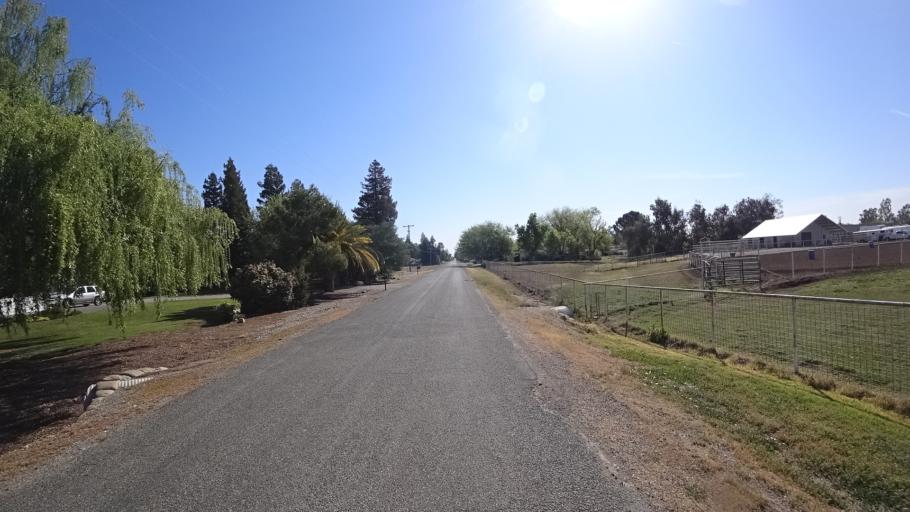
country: US
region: California
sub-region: Glenn County
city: Willows
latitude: 39.5334
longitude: -122.2108
